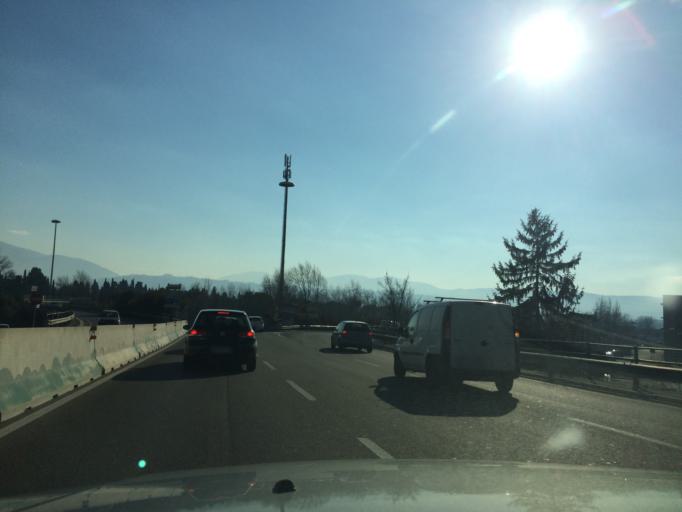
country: IT
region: Umbria
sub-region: Provincia di Terni
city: Terni
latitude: 42.5698
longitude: 12.6305
